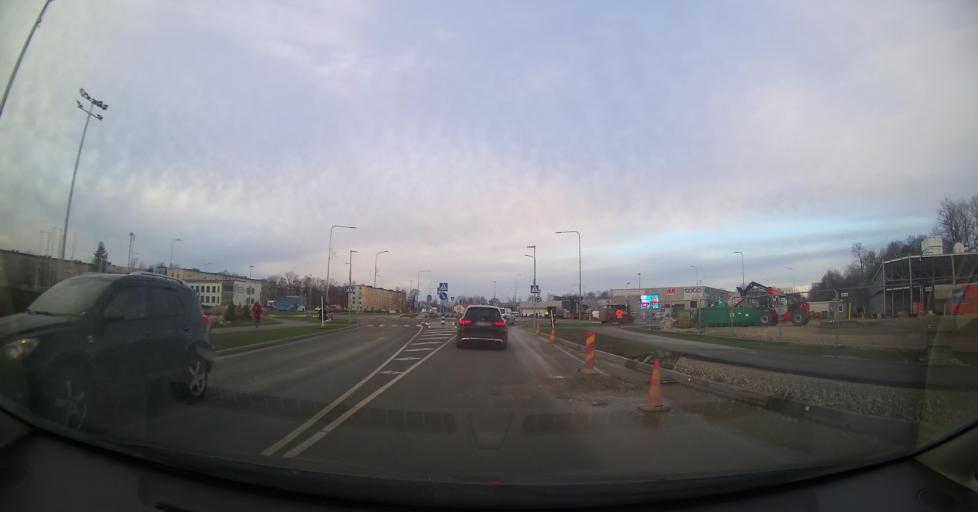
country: EE
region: Ida-Virumaa
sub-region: Johvi vald
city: Johvi
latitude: 59.3503
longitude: 27.4192
